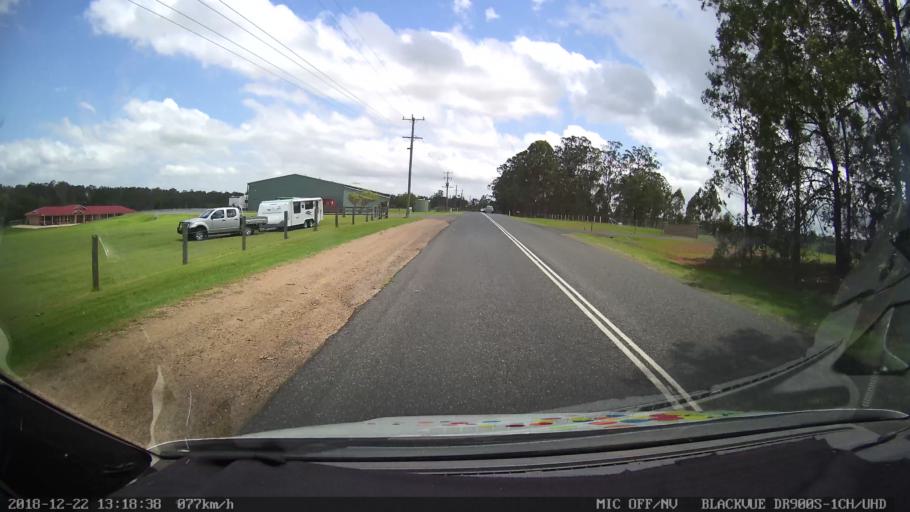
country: AU
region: New South Wales
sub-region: Clarence Valley
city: South Grafton
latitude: -29.7486
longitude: 152.9335
